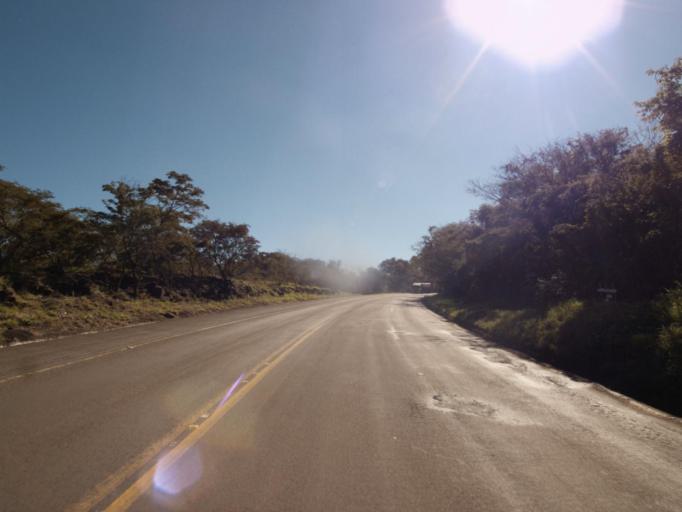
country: AR
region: Misiones
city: Bernardo de Irigoyen
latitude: -26.7848
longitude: -53.4602
